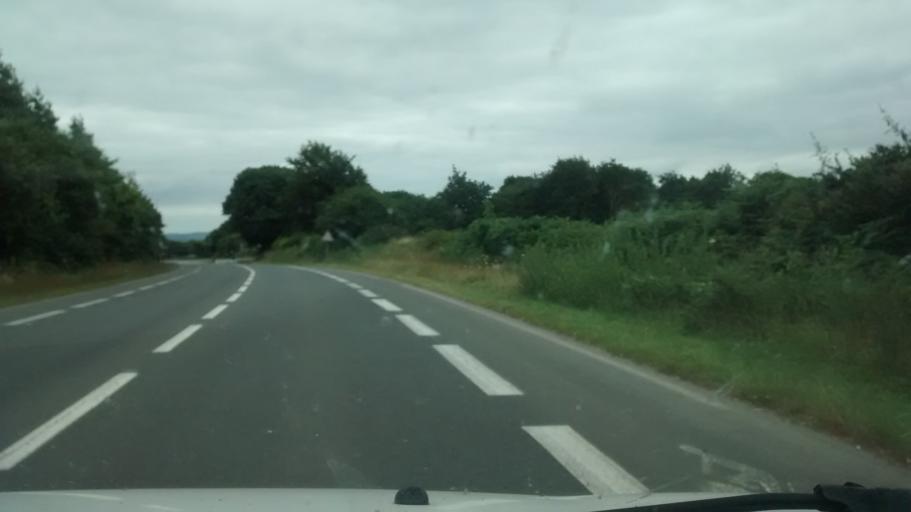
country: FR
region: Brittany
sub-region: Departement du Finistere
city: Plougastel-Daoulas
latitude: 48.3738
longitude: -4.3802
